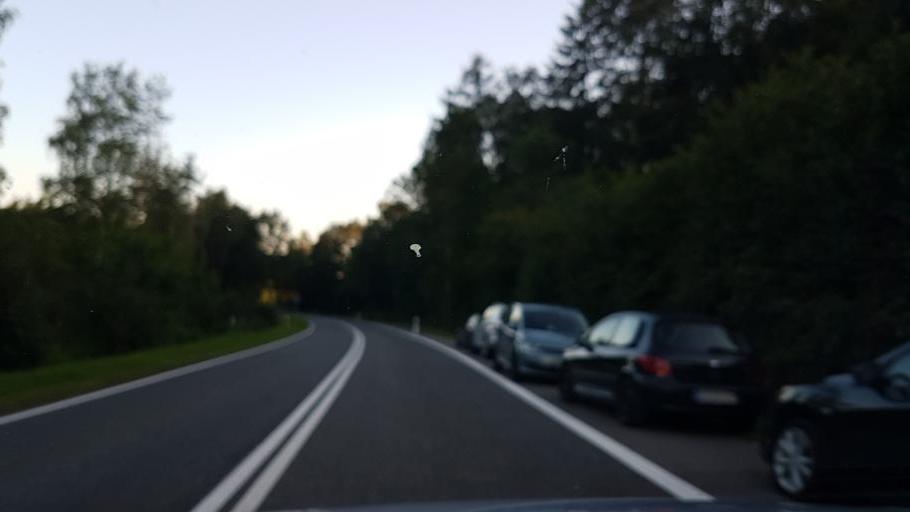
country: DE
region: Saarland
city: Weiskirchen
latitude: 49.5236
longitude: 6.8292
